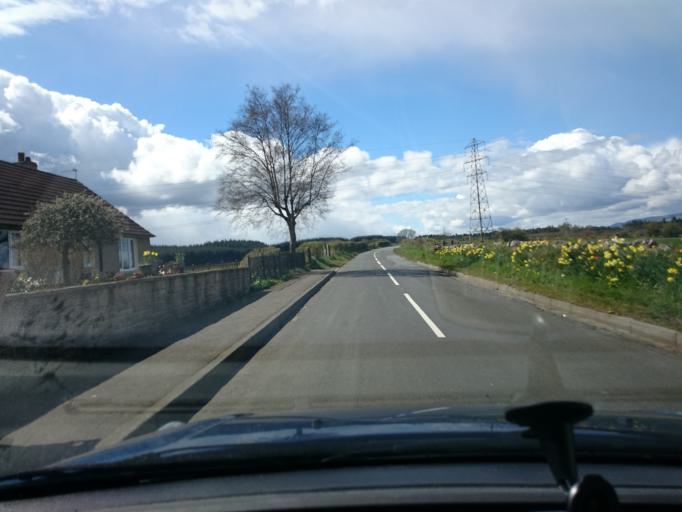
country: GB
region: Scotland
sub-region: Falkirk
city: Larbert
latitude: 55.9825
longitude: -3.8467
